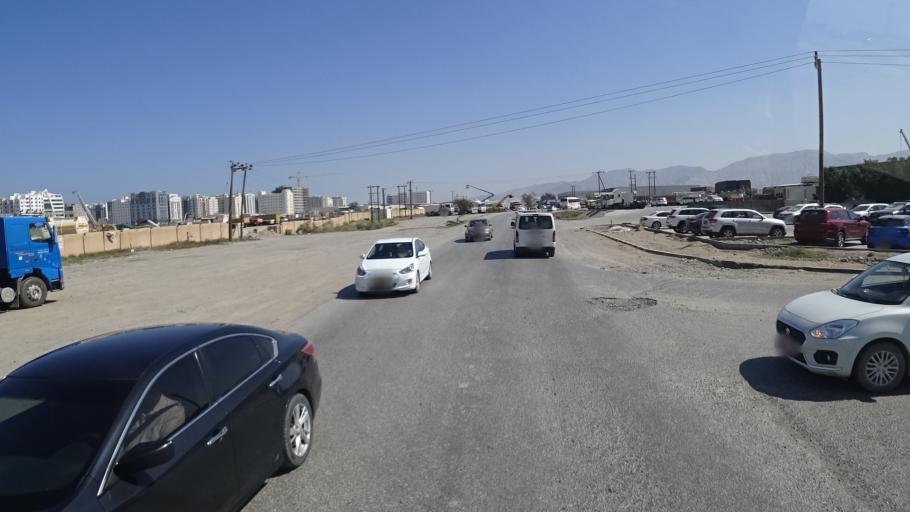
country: OM
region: Muhafazat Masqat
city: Bawshar
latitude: 23.5800
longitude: 58.3626
